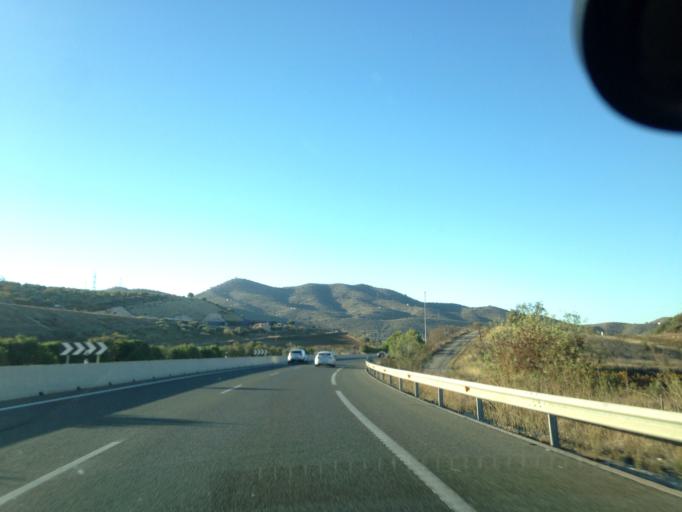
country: ES
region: Andalusia
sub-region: Provincia de Malaga
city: Casabermeja
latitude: 36.9130
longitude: -4.4436
